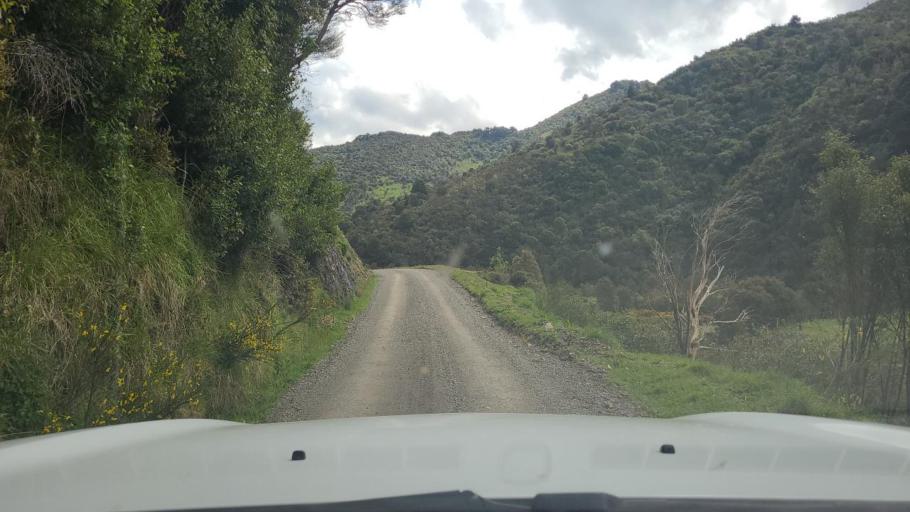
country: NZ
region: Wellington
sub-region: Masterton District
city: Masterton
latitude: -40.9345
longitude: 175.4868
